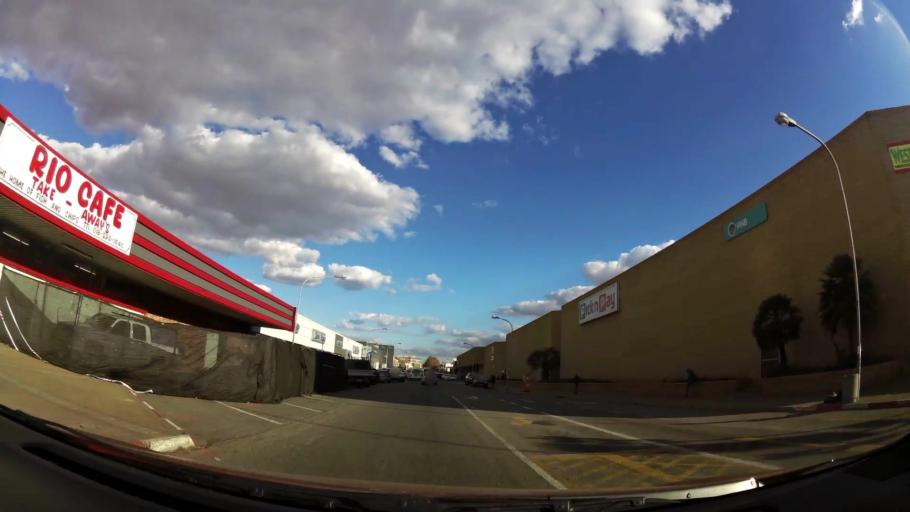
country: ZA
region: North-West
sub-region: Dr Kenneth Kaunda District Municipality
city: Potchefstroom
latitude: -26.7076
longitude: 27.0977
